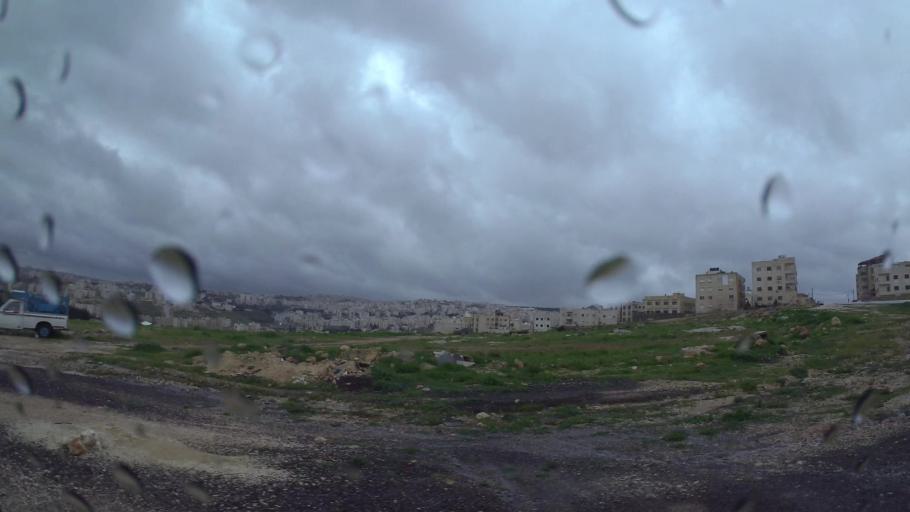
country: JO
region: Amman
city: Al Jubayhah
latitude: 32.0451
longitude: 35.8964
